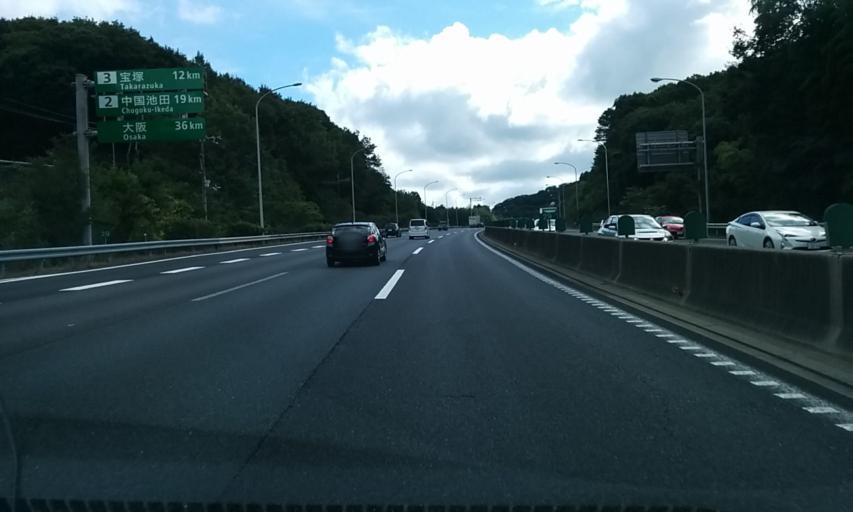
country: JP
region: Hyogo
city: Sandacho
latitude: 34.8383
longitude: 135.2455
